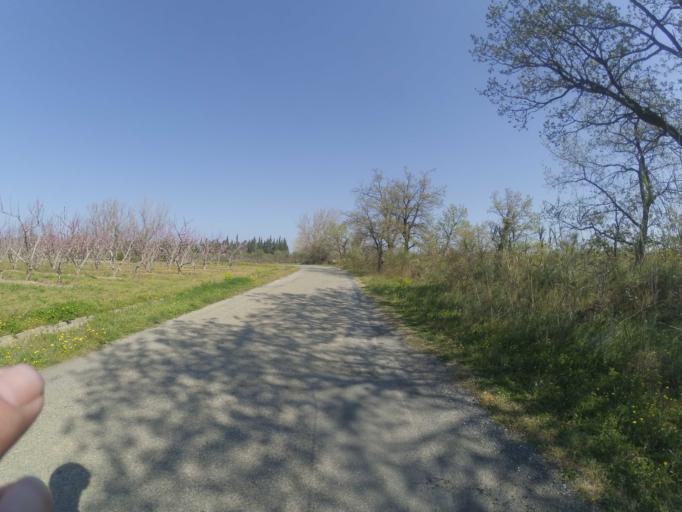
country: FR
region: Languedoc-Roussillon
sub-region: Departement des Pyrenees-Orientales
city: Pezilla-la-Riviere
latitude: 42.6759
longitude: 2.7513
